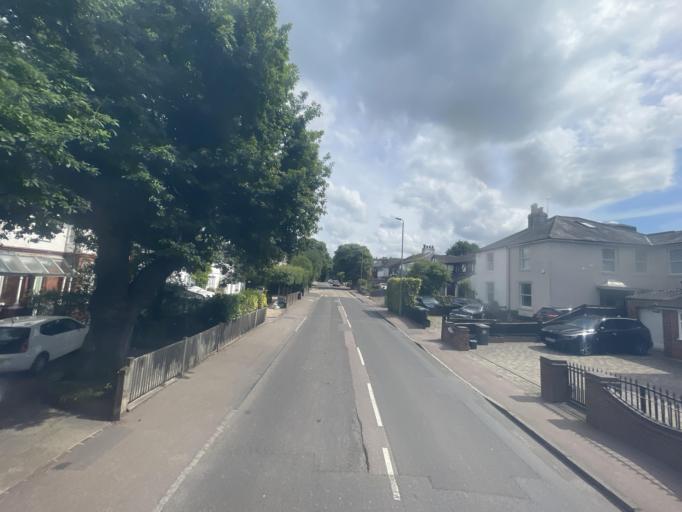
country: GB
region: England
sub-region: Greater London
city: West Wickham
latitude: 51.3609
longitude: 0.0290
